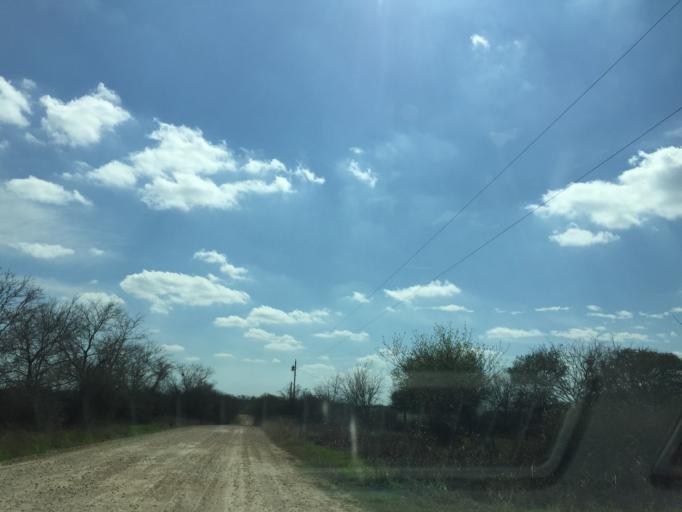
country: US
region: Texas
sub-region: Milam County
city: Thorndale
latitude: 30.5638
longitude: -97.1957
